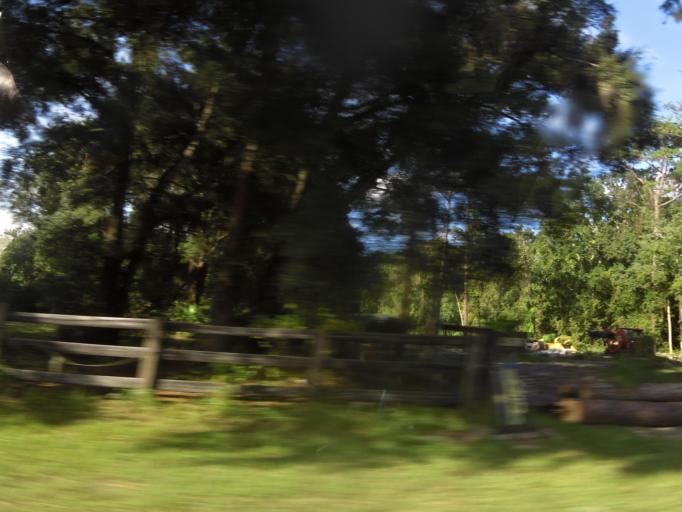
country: US
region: Florida
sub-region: Saint Johns County
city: Saint Augustine
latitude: 29.9057
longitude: -81.4976
